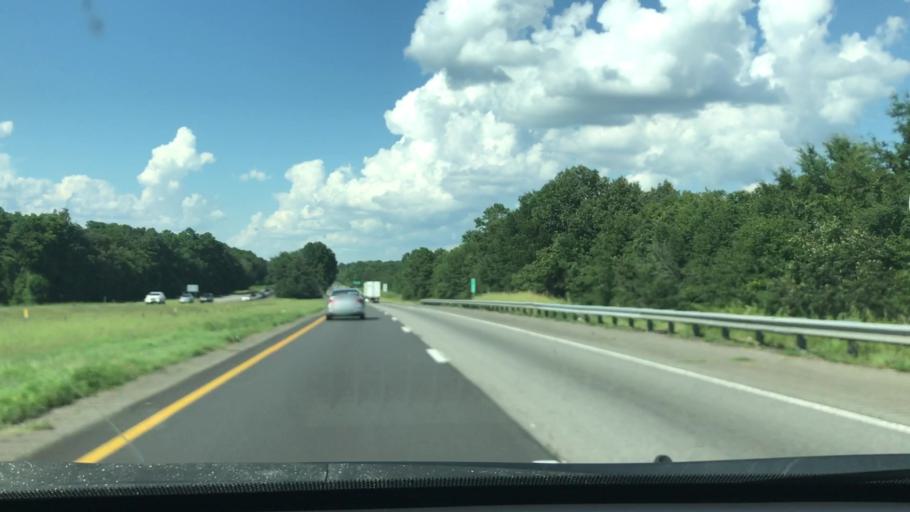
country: US
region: South Carolina
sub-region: Orangeburg County
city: Holly Hill
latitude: 33.5251
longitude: -80.4276
